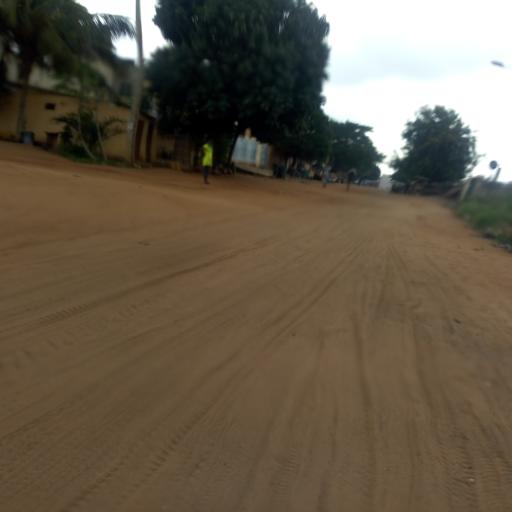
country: TG
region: Maritime
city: Lome
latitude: 6.1906
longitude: 1.2581
